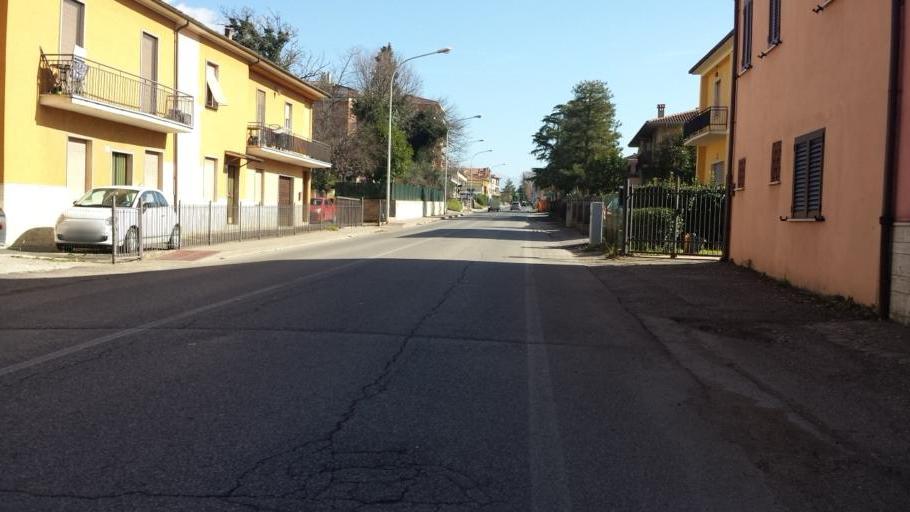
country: IT
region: Umbria
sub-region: Provincia di Terni
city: San Gemini
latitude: 42.5903
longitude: 12.5790
